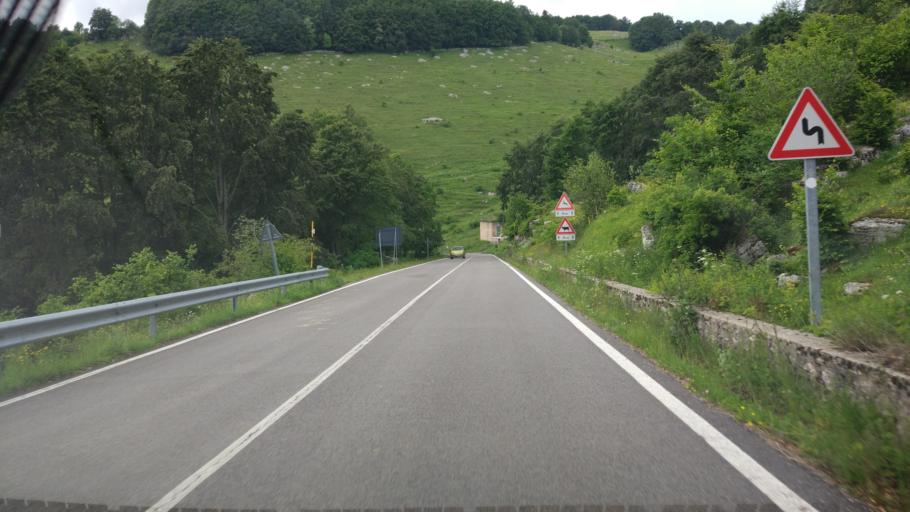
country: IT
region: Veneto
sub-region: Provincia di Verona
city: Bosco Chiesanuova
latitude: 45.6687
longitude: 11.0554
